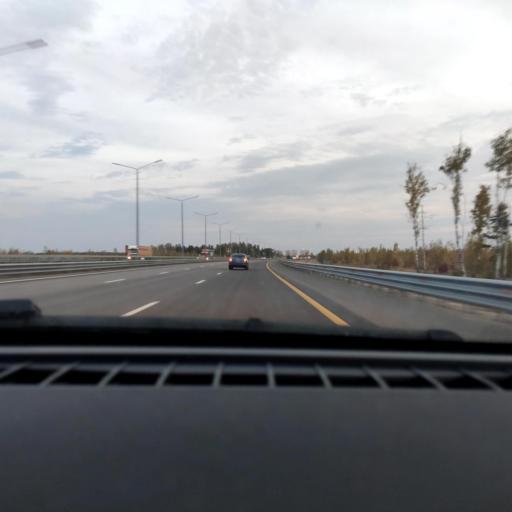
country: RU
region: Voronezj
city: Somovo
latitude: 51.7661
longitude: 39.3047
